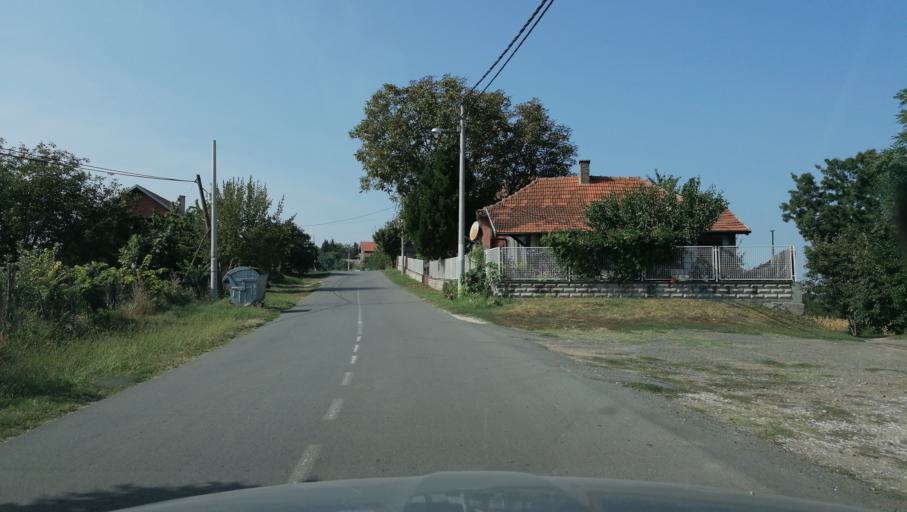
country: RS
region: Central Serbia
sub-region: Belgrade
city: Sopot
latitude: 44.5998
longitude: 20.6057
